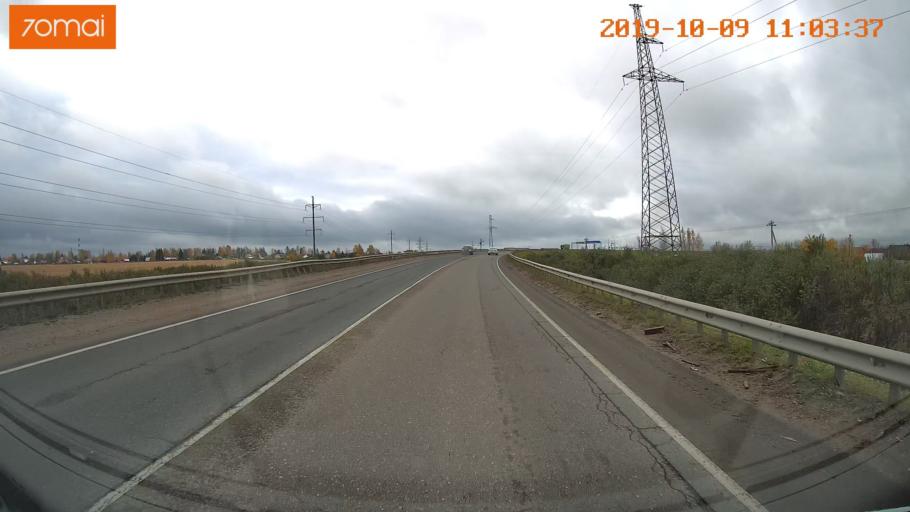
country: RU
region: Vologda
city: Vologda
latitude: 59.2188
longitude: 39.7739
